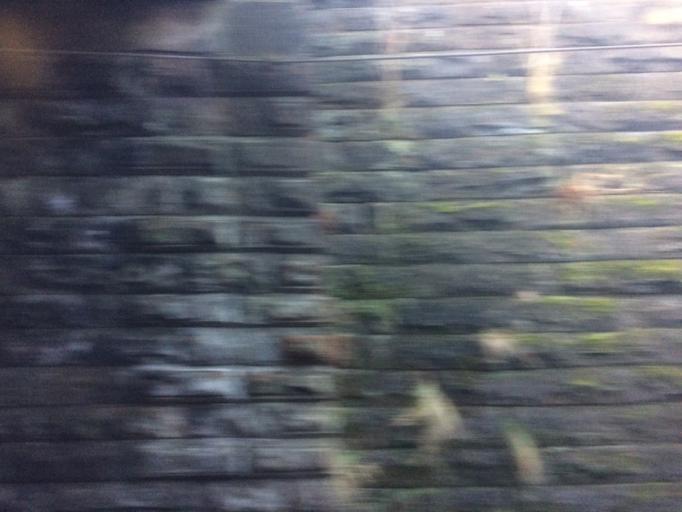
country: GB
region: Scotland
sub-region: Glasgow City
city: Glasgow
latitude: 55.8280
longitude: -4.2606
